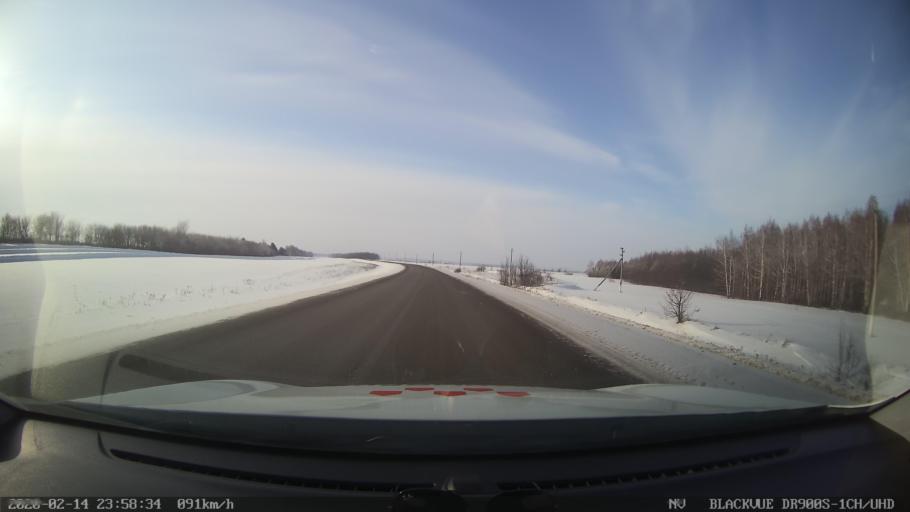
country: RU
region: Tatarstan
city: Kuybyshevskiy Zaton
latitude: 55.3414
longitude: 49.0844
